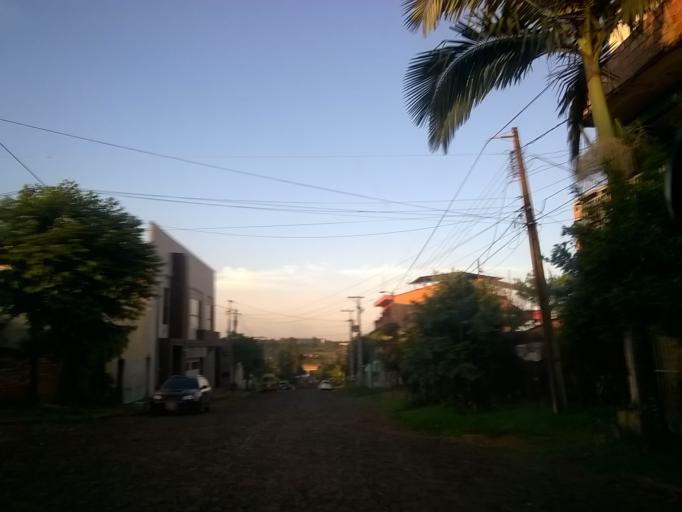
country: PY
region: Alto Parana
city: Ciudad del Este
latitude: -25.5067
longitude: -54.6520
